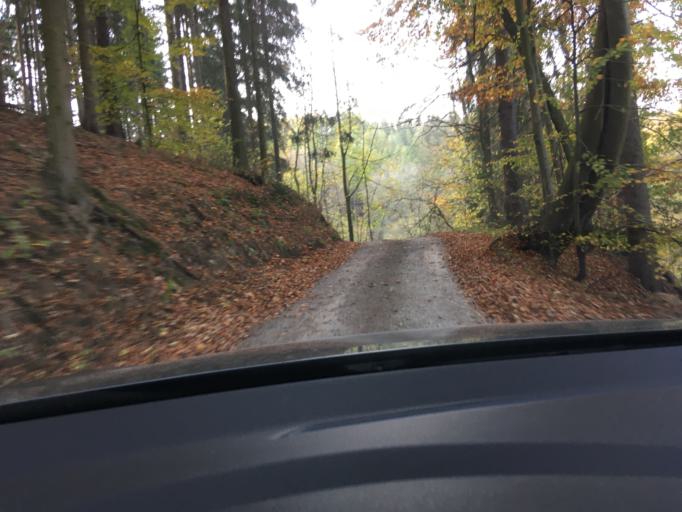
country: DE
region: Saxony
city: Barenstein
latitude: 50.8241
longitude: 13.8257
